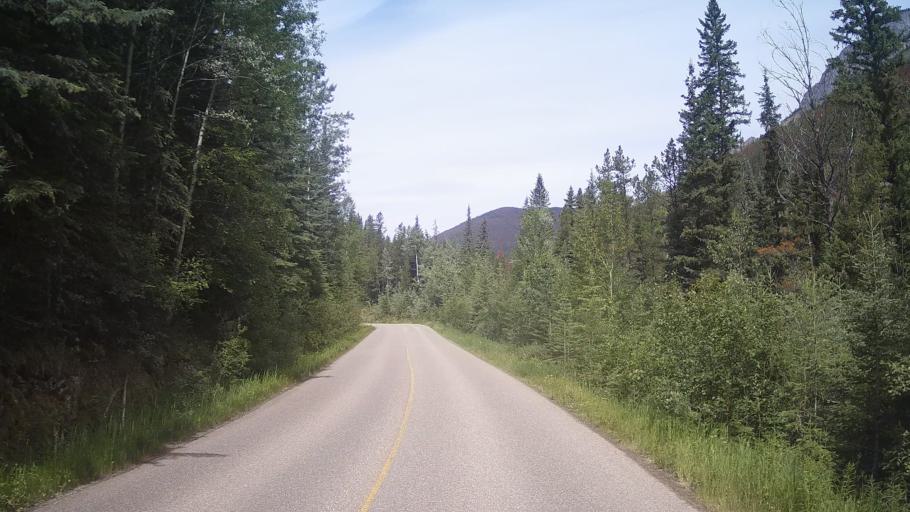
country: CA
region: Alberta
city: Hinton
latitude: 53.1773
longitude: -117.8330
